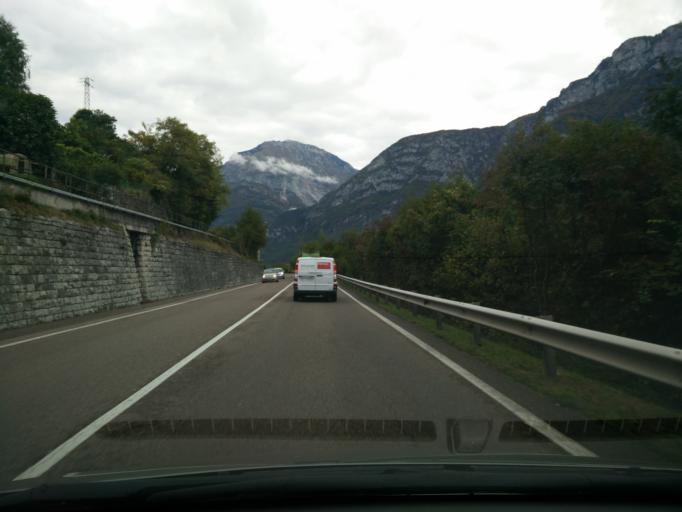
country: IT
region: Veneto
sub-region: Provincia di Belluno
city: Soverzene
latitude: 46.2334
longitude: 12.2931
